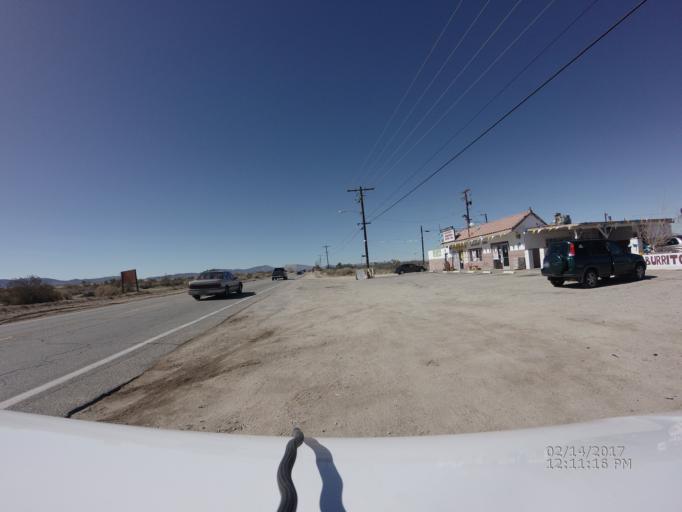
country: US
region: California
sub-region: Los Angeles County
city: Littlerock
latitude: 34.5798
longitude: -117.9733
